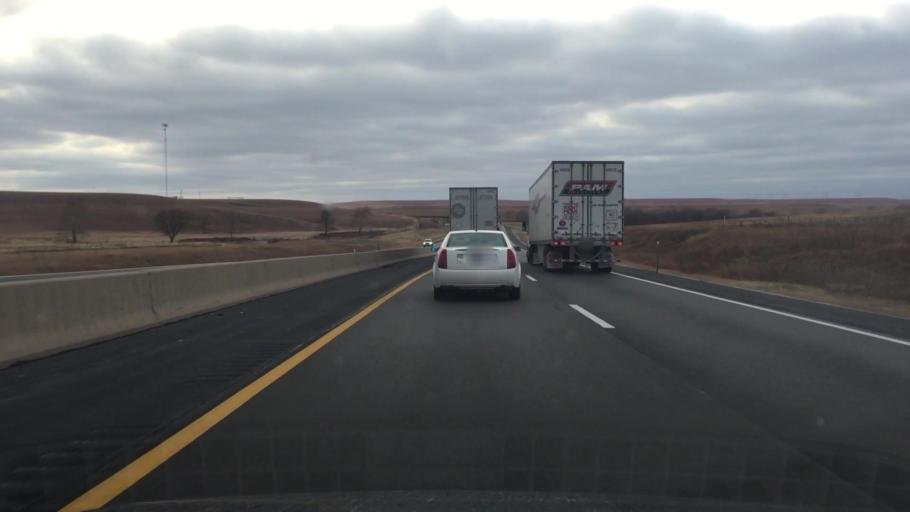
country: US
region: Kansas
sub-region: Chase County
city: Cottonwood Falls
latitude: 38.1771
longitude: -96.4663
